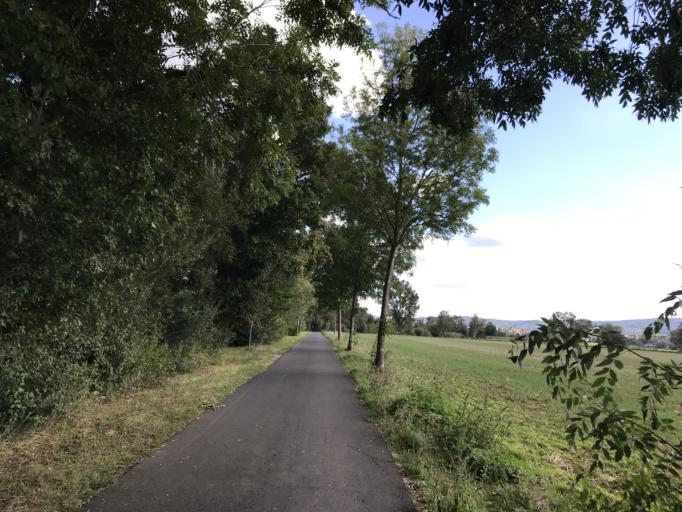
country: DE
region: Hesse
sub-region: Regierungsbezirk Kassel
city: Eschwege
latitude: 51.2067
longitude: 10.0363
